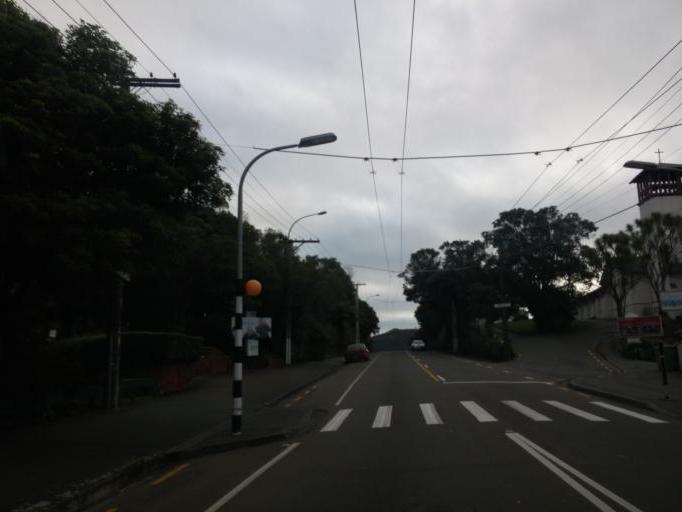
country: NZ
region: Wellington
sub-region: Wellington City
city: Kelburn
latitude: -41.2829
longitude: 174.7445
